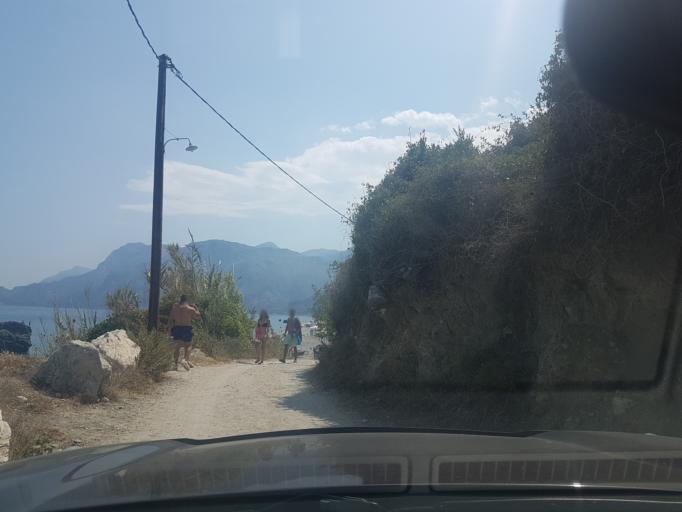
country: GR
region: Central Greece
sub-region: Nomos Evvoias
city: Kymi
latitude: 38.6714
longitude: 23.9187
